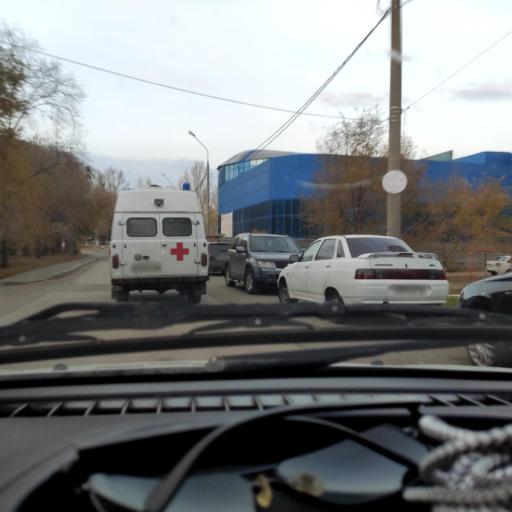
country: RU
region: Samara
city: Zhigulevsk
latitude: 53.4806
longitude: 49.4716
